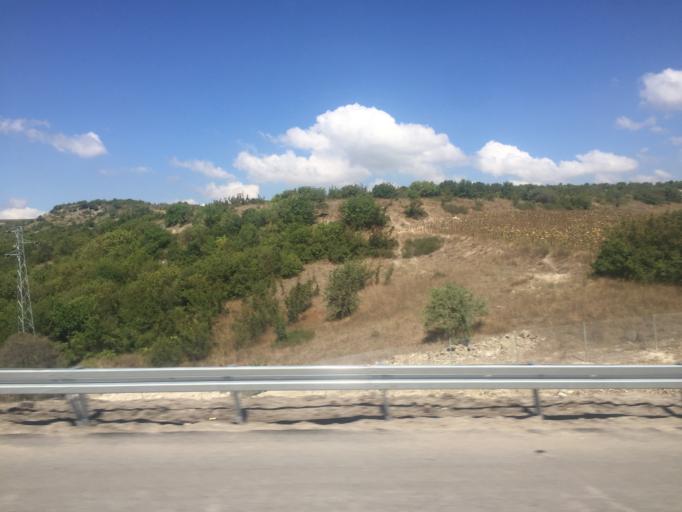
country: TR
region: Balikesir
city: Gobel
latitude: 39.9724
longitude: 28.1646
